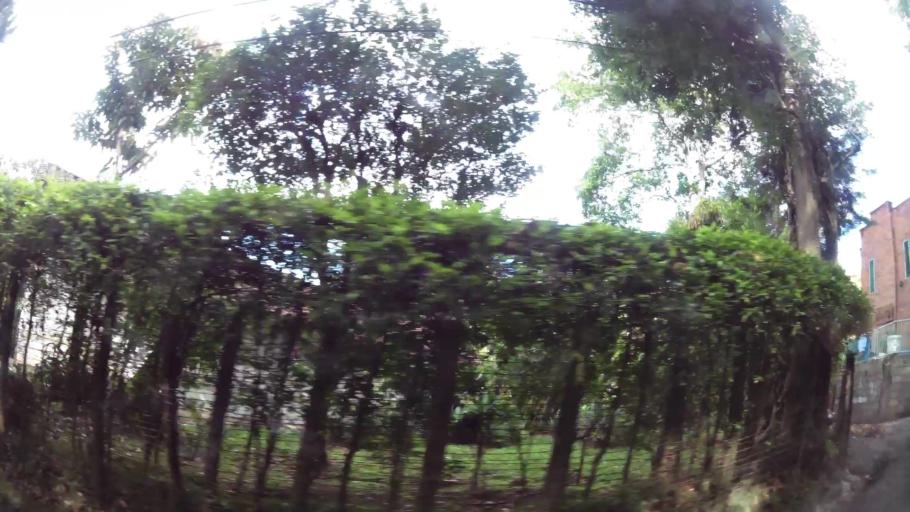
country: CO
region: Antioquia
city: Sabaneta
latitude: 6.1494
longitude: -75.6063
